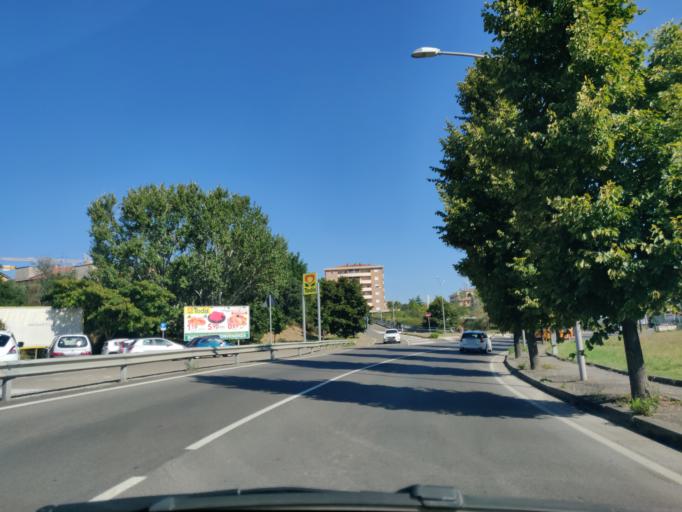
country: IT
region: Latium
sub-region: Provincia di Viterbo
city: Viterbo
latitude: 42.4236
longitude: 12.0935
